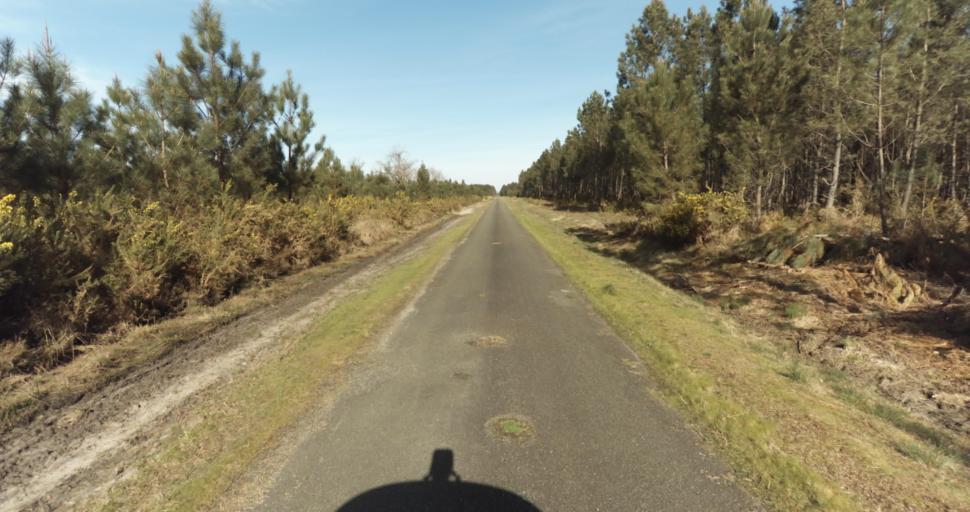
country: FR
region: Aquitaine
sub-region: Departement des Landes
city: Roquefort
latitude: 44.1243
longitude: -0.3080
